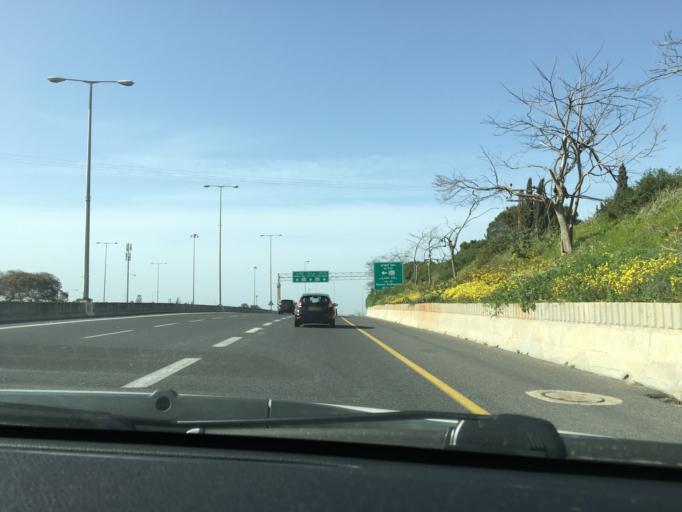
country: IL
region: Tel Aviv
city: Ramat HaSharon
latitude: 32.1328
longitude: 34.8370
